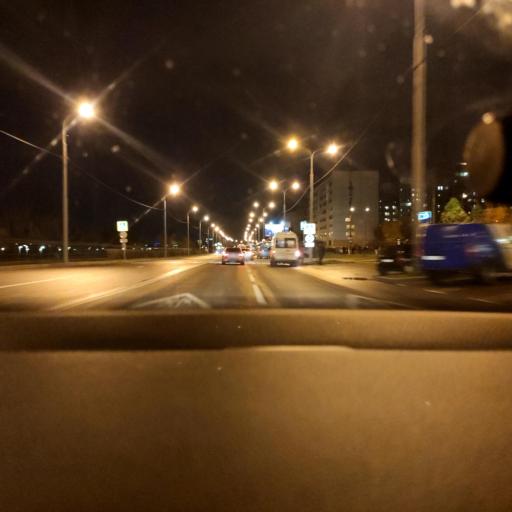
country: RU
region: Moscow
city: Kuz'minki
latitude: 55.6718
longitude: 37.7947
